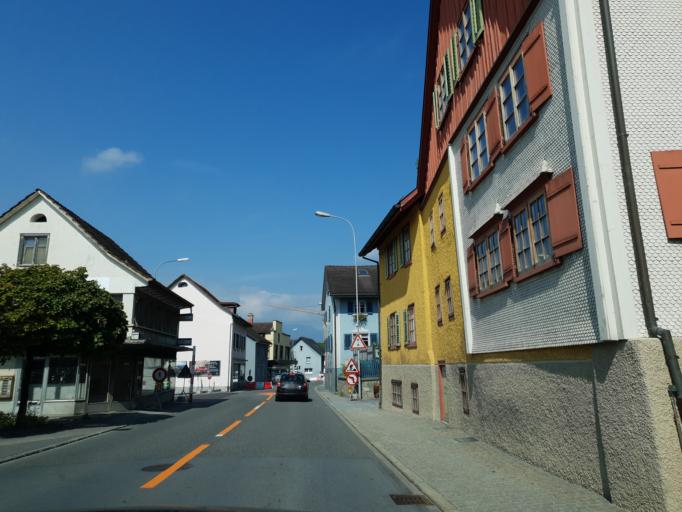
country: LI
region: Schaan
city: Schaan
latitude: 47.1627
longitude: 9.5086
